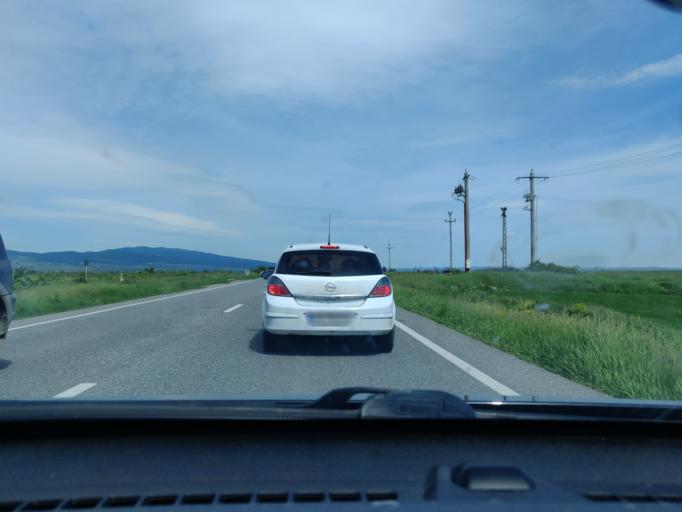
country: RO
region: Vrancea
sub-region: Oras Odobesti
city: Unirea
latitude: 45.7542
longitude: 27.1308
